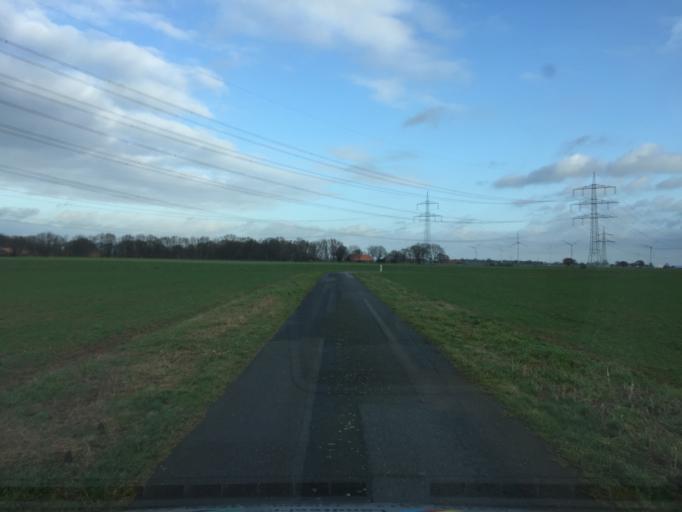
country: DE
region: Lower Saxony
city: Steyerberg
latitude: 52.5444
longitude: 9.0228
